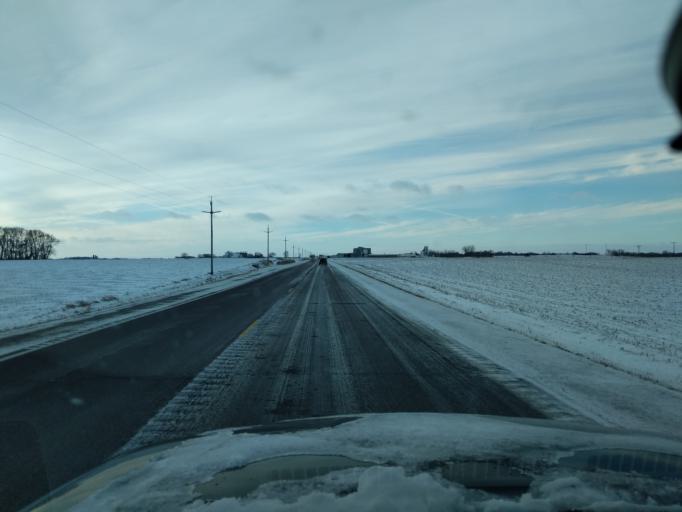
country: US
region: Minnesota
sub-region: Renville County
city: Hector
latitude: 44.7315
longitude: -94.5859
